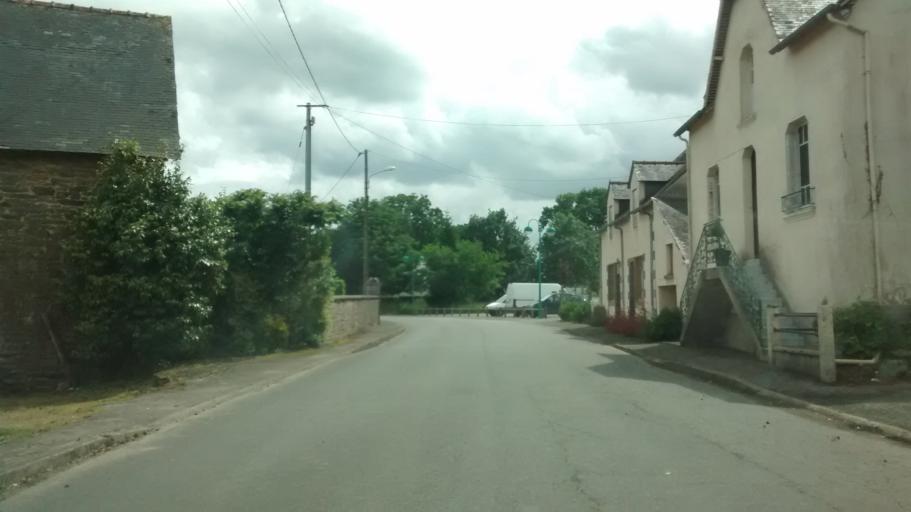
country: FR
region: Brittany
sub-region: Departement du Morbihan
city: Ruffiac
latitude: 47.8379
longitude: -2.2241
